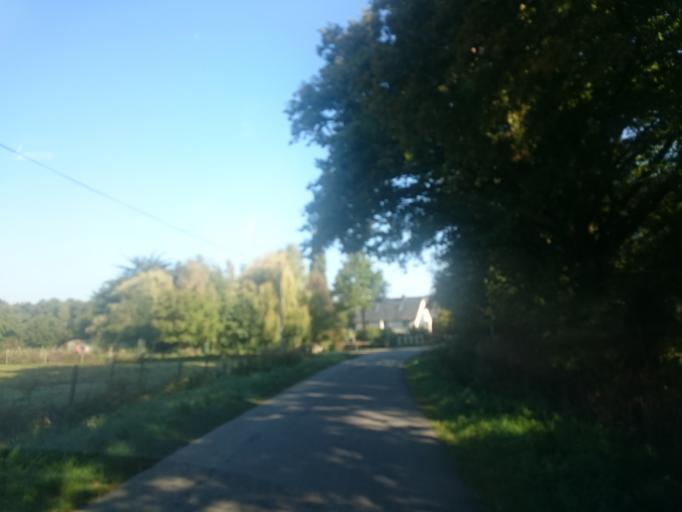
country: FR
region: Brittany
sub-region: Departement d'Ille-et-Vilaine
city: Chanteloup
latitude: 47.9323
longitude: -1.5852
